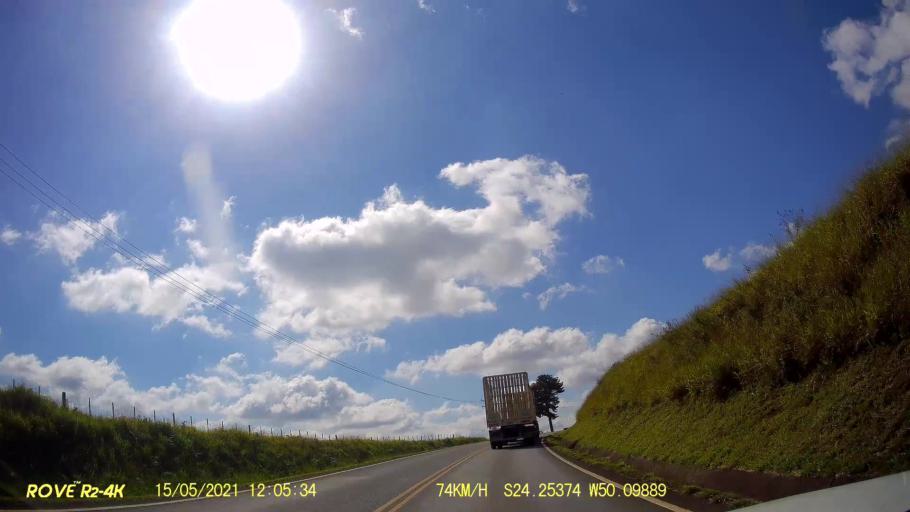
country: BR
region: Parana
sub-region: Pirai Do Sul
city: Pirai do Sul
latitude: -24.2529
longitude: -50.0981
